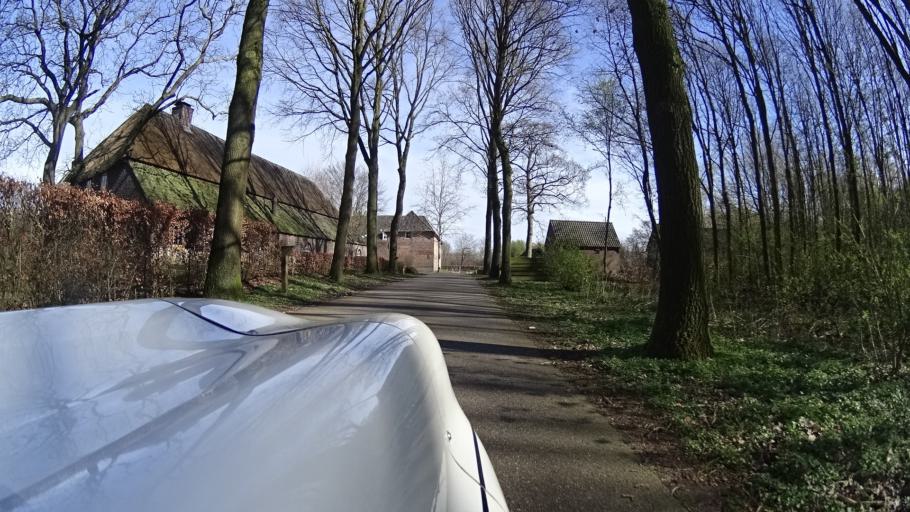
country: NL
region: North Brabant
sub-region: Gemeente Mill en Sint Hubert
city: Wilbertoord
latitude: 51.7122
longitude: 5.7799
